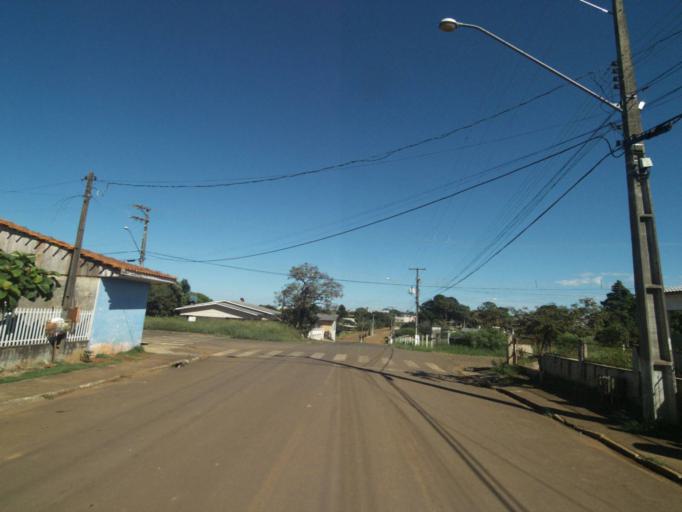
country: BR
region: Parana
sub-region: Pinhao
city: Pinhao
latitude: -25.8387
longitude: -52.0278
